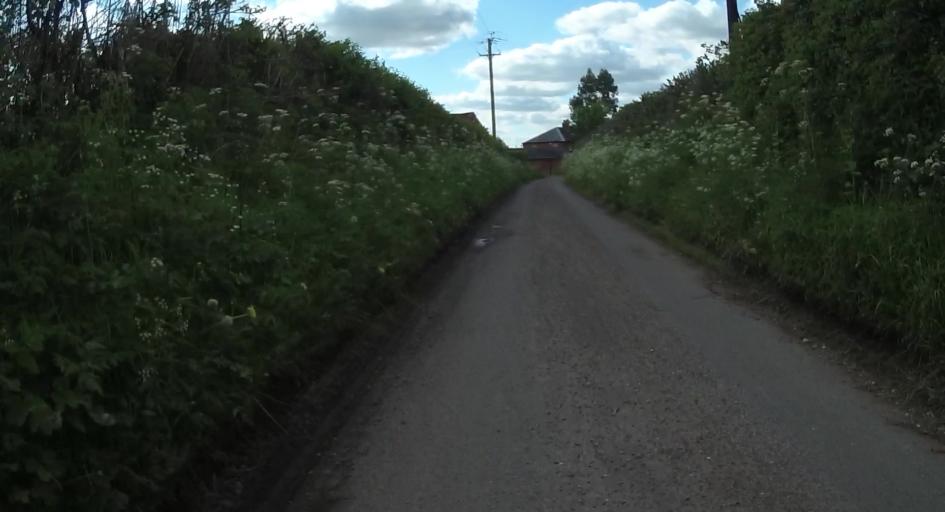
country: GB
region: England
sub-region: Wokingham
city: Swallowfield
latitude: 51.3629
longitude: -0.9772
